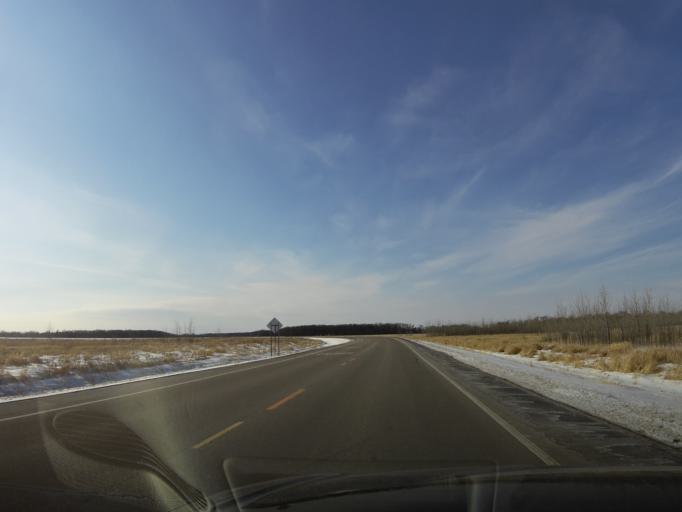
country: US
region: North Dakota
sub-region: Walsh County
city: Grafton
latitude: 48.4131
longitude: -97.1129
